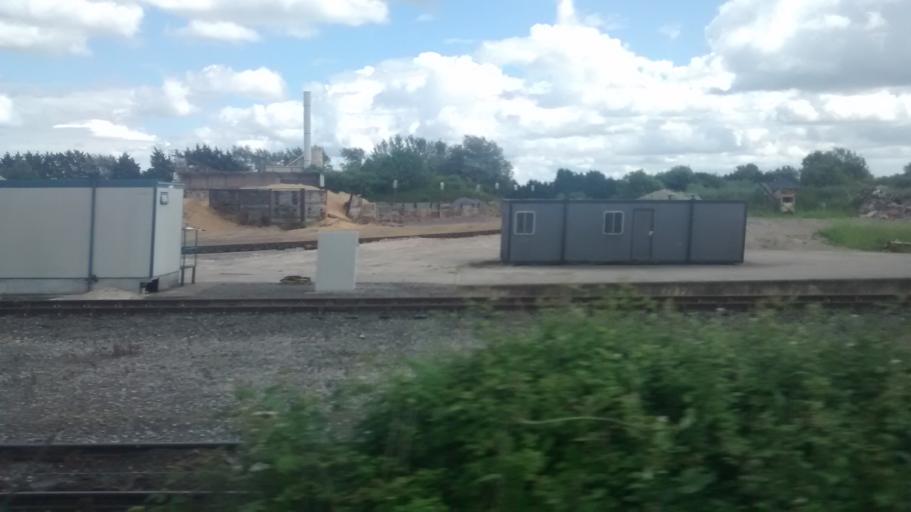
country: GB
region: England
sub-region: Cambridgeshire
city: Ely
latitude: 52.4038
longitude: 0.2892
